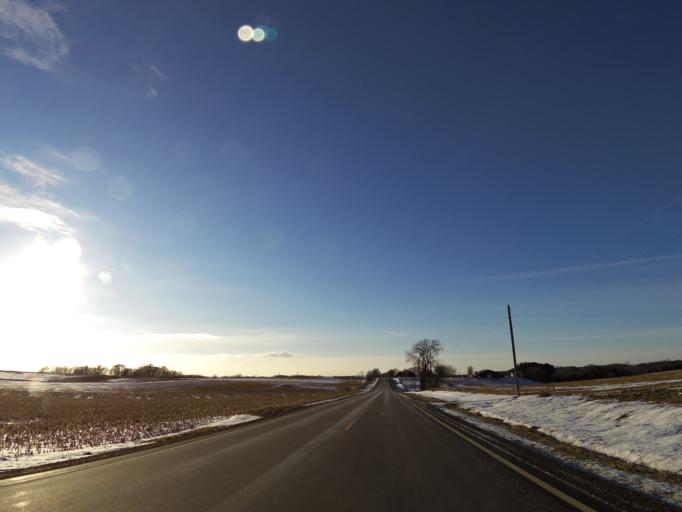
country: US
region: Minnesota
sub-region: Dakota County
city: Hastings
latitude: 44.7901
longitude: -92.8545
